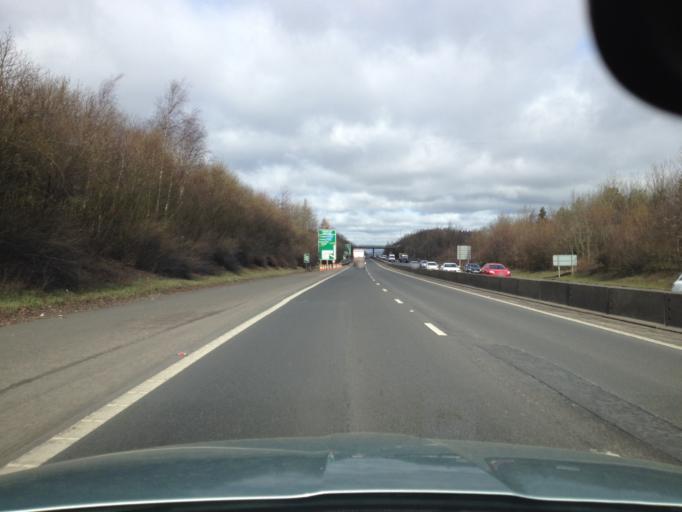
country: GB
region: Scotland
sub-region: Edinburgh
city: Colinton
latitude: 55.9039
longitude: -3.2741
